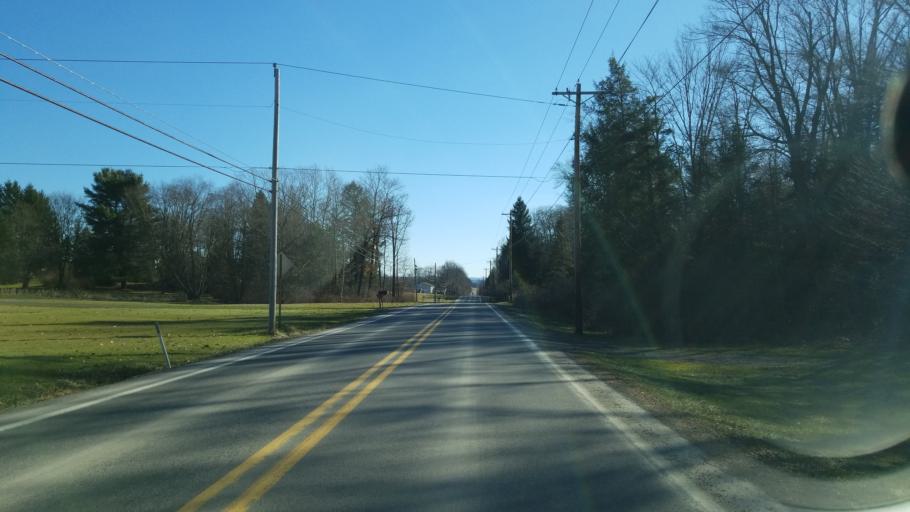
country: US
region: Pennsylvania
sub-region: Jefferson County
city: Falls Creek
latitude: 41.1736
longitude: -78.8348
